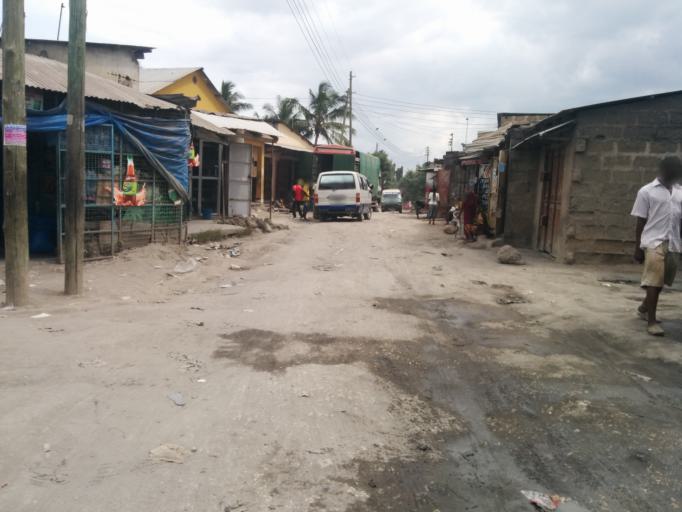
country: TZ
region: Dar es Salaam
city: Dar es Salaam
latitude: -6.8691
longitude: 39.2435
